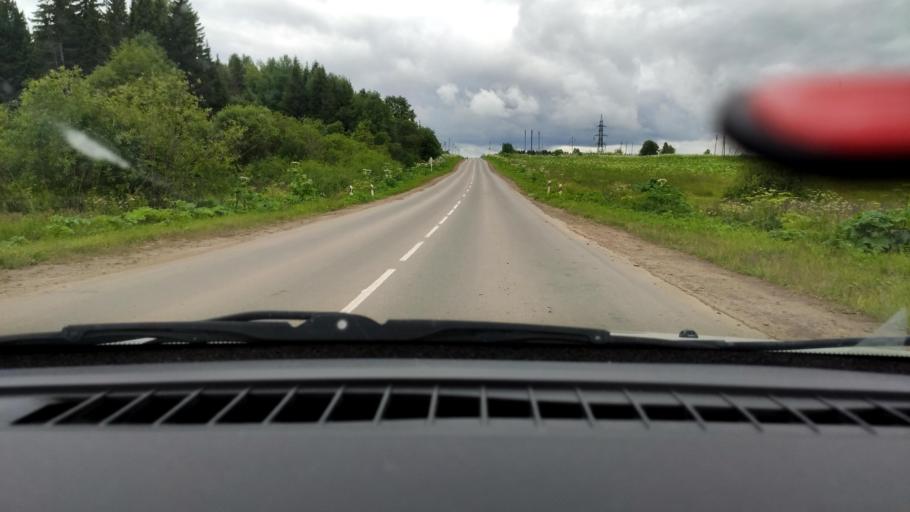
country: RU
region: Perm
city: Chaykovskaya
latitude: 58.1221
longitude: 55.5618
